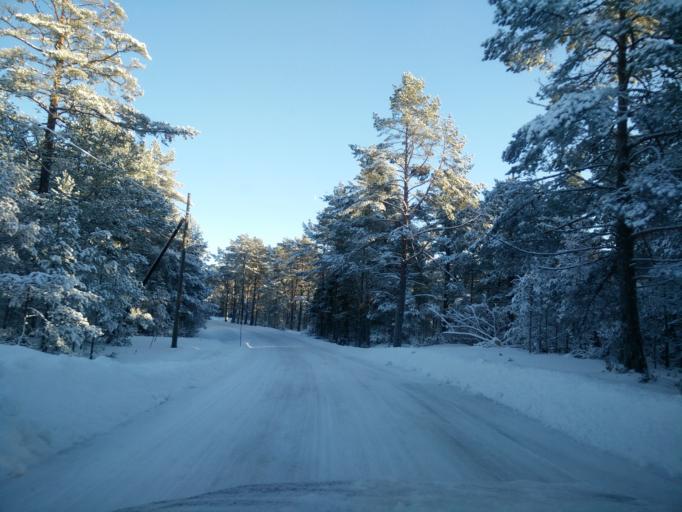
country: SE
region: Vaesternorrland
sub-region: Sundsvalls Kommun
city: Njurundabommen
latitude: 62.2332
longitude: 17.6439
